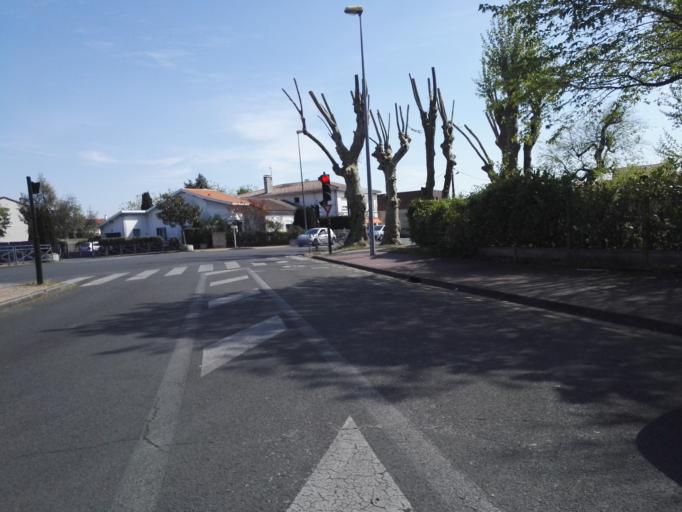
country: FR
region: Aquitaine
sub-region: Departement de la Gironde
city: Talence
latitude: 44.8123
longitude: -0.5825
